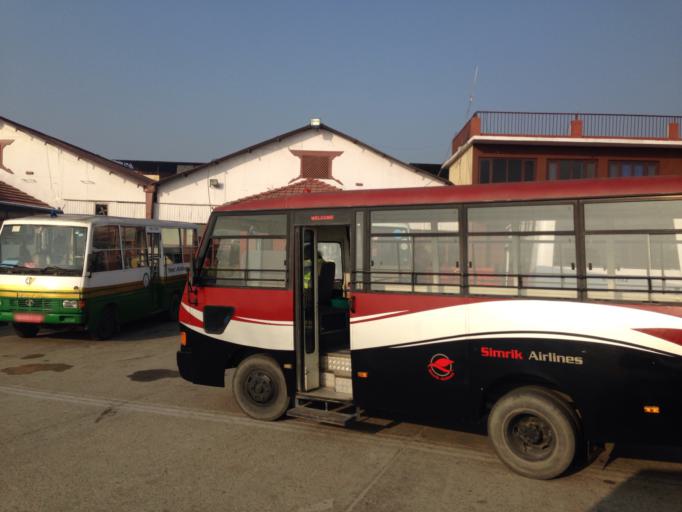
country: NP
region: Central Region
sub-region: Bagmati Zone
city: Kathmandu
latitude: 27.7023
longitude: 85.3601
